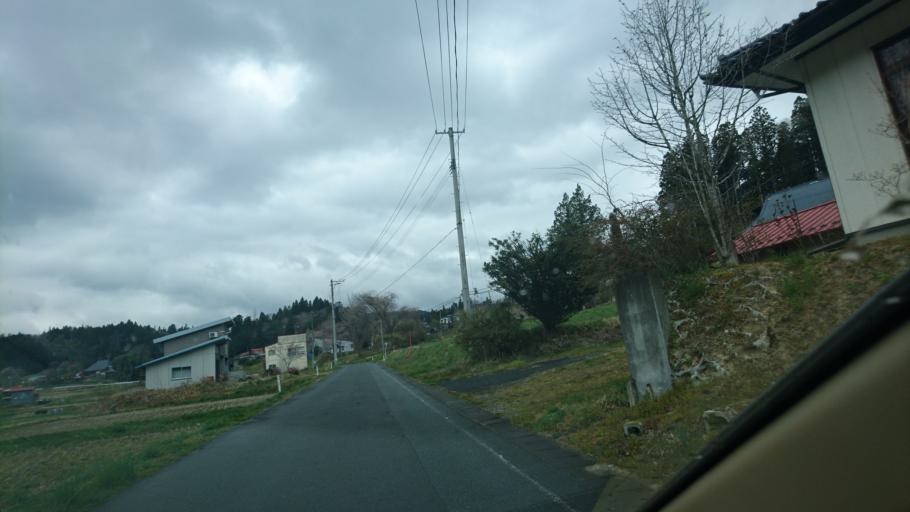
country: JP
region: Iwate
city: Ichinoseki
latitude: 38.9442
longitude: 141.3234
